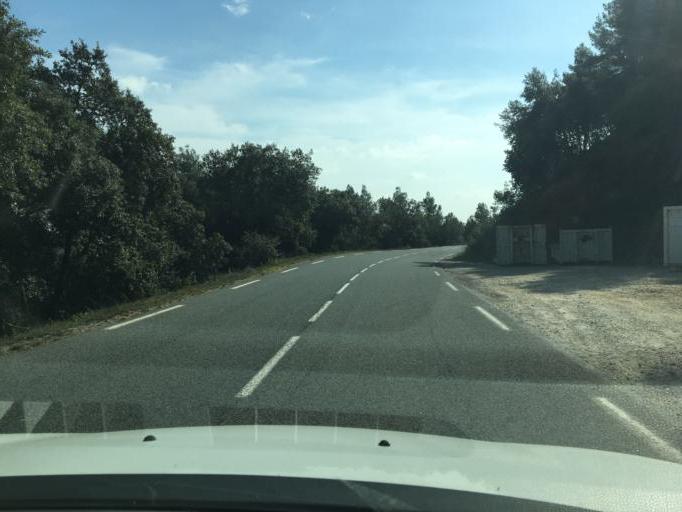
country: FR
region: Provence-Alpes-Cote d'Azur
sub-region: Departement du Var
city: Bargemon
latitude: 43.6102
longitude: 6.5515
